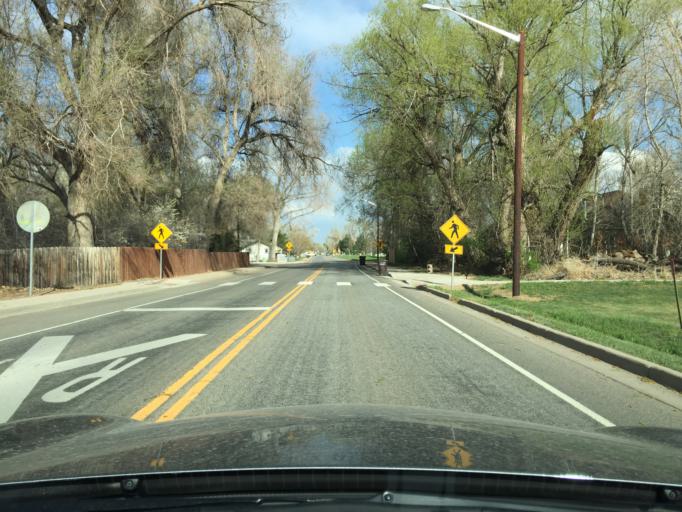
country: US
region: Colorado
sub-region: Boulder County
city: Niwot
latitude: 40.1016
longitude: -105.1743
